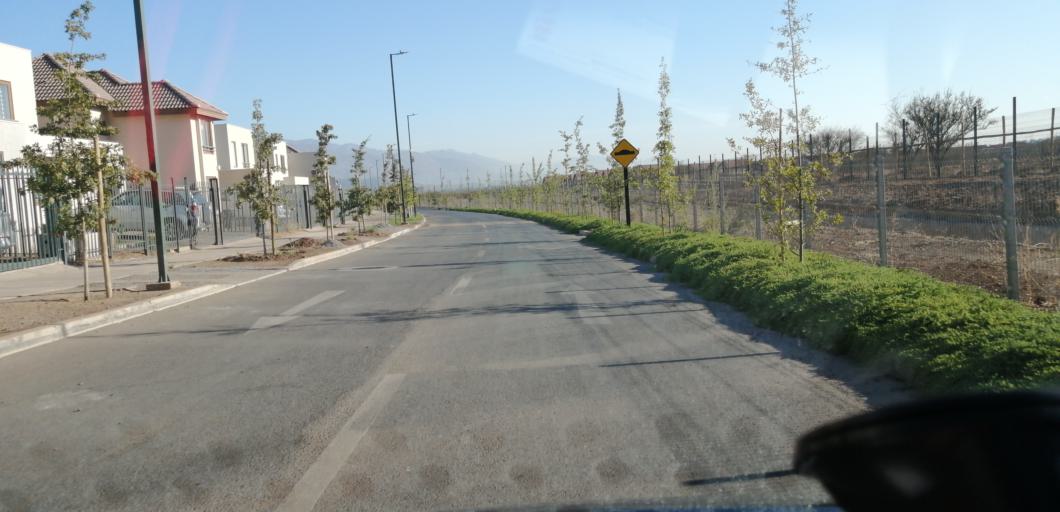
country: CL
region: Santiago Metropolitan
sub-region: Provincia de Santiago
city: Lo Prado
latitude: -33.4685
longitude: -70.8597
